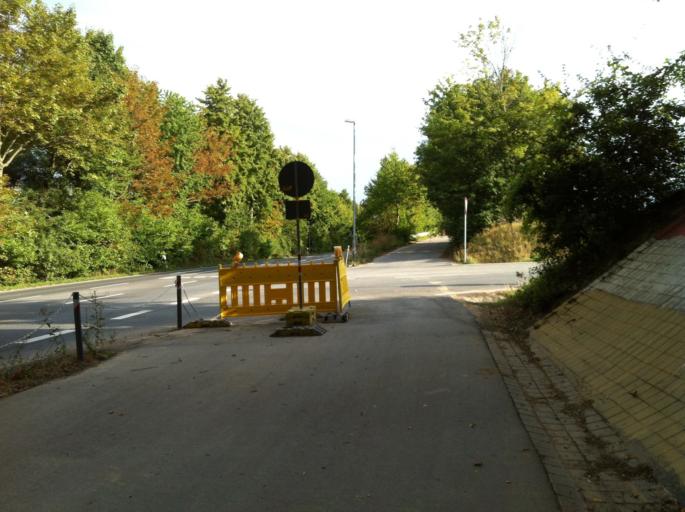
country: DE
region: Rheinland-Pfalz
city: Mainz
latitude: 49.9851
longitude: 8.2309
